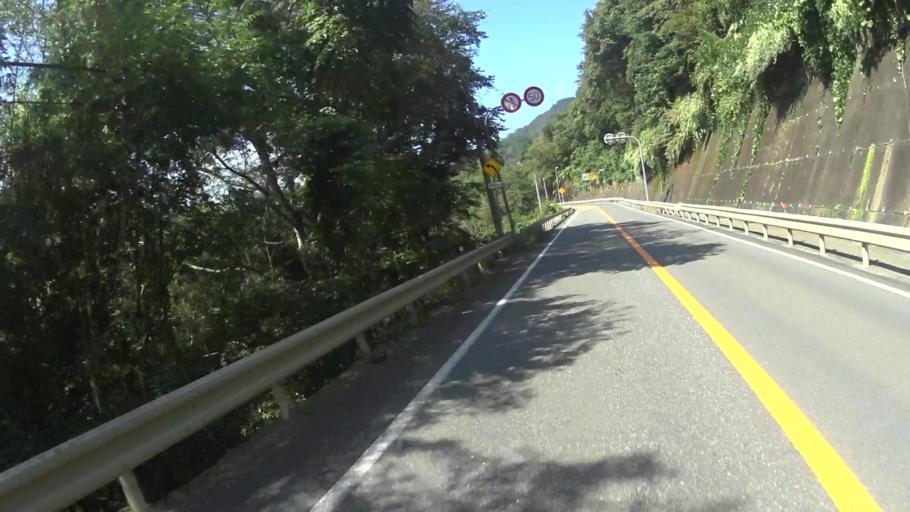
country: JP
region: Kyoto
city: Ayabe
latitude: 35.2983
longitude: 135.3213
